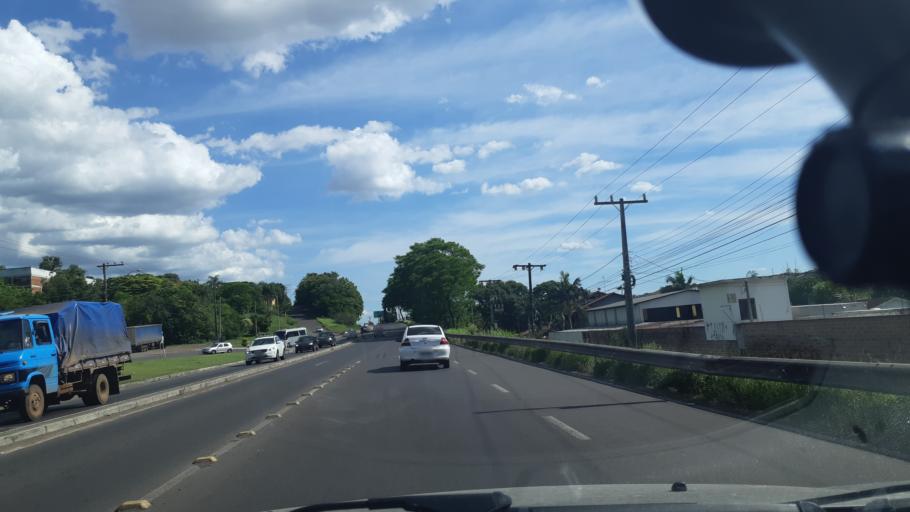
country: BR
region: Rio Grande do Sul
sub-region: Estancia Velha
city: Estancia Velha
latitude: -29.6499
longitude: -51.1443
